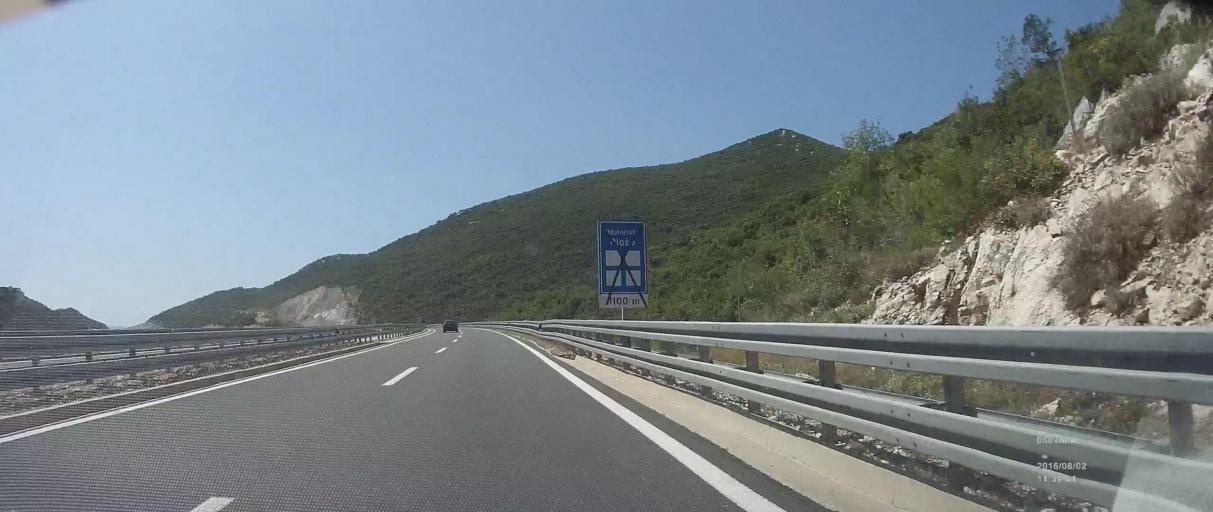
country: HR
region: Dubrovacko-Neretvanska
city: Komin
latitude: 43.0834
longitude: 17.4905
